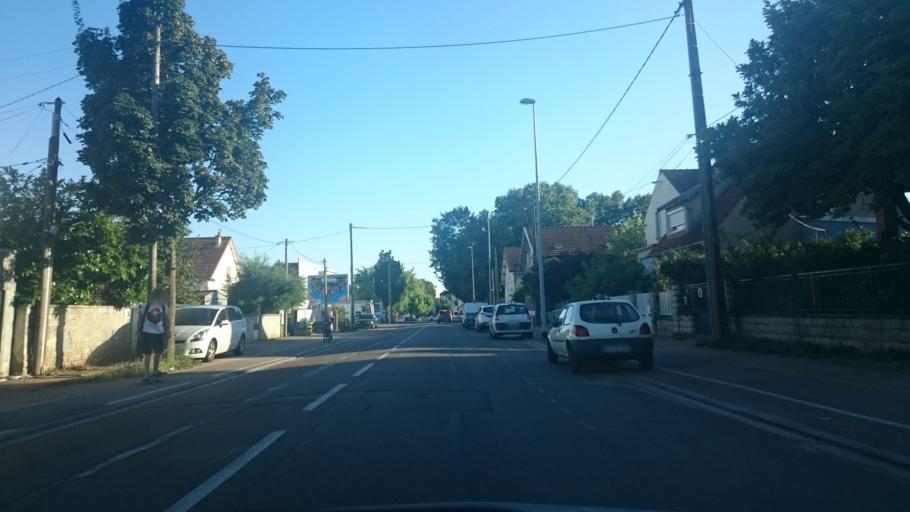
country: FR
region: Bourgogne
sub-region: Departement de la Cote-d'Or
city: Saint-Apollinaire
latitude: 47.3382
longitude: 5.0568
